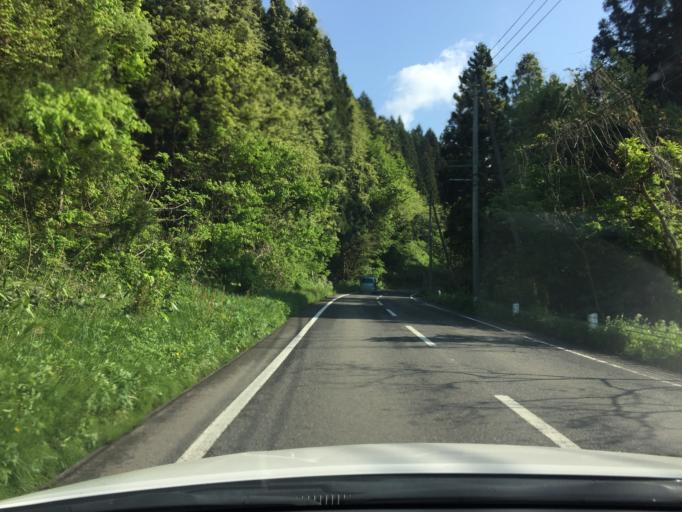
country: JP
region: Fukushima
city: Kitakata
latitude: 37.6870
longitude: 139.5755
